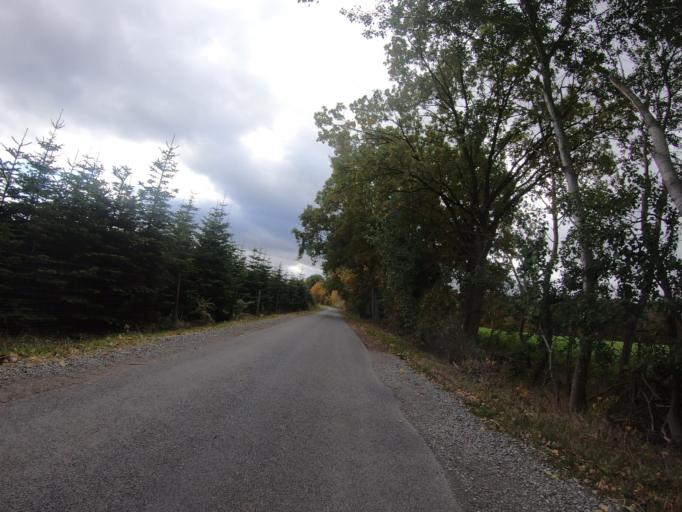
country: DE
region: Lower Saxony
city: Ribbesbuttel
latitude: 52.4159
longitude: 10.4813
